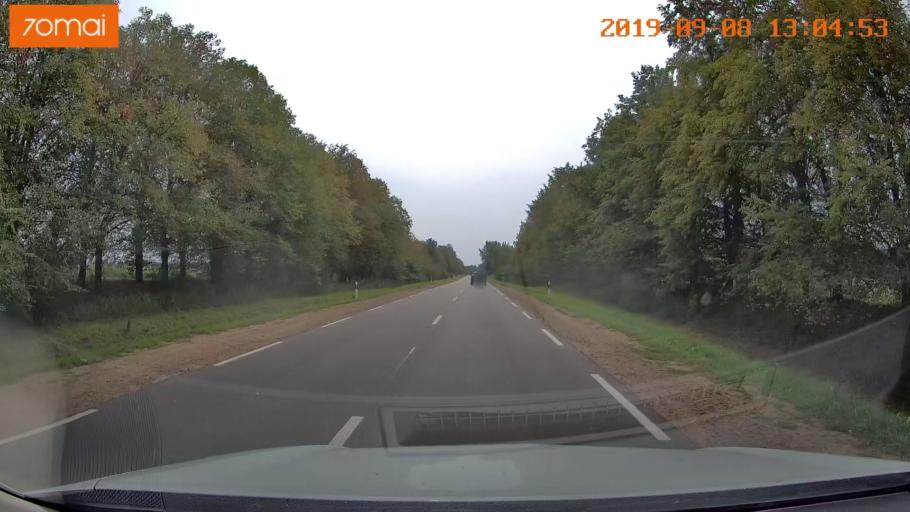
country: LT
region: Kauno apskritis
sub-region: Kauno rajonas
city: Karmelava
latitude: 54.8614
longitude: 24.2356
